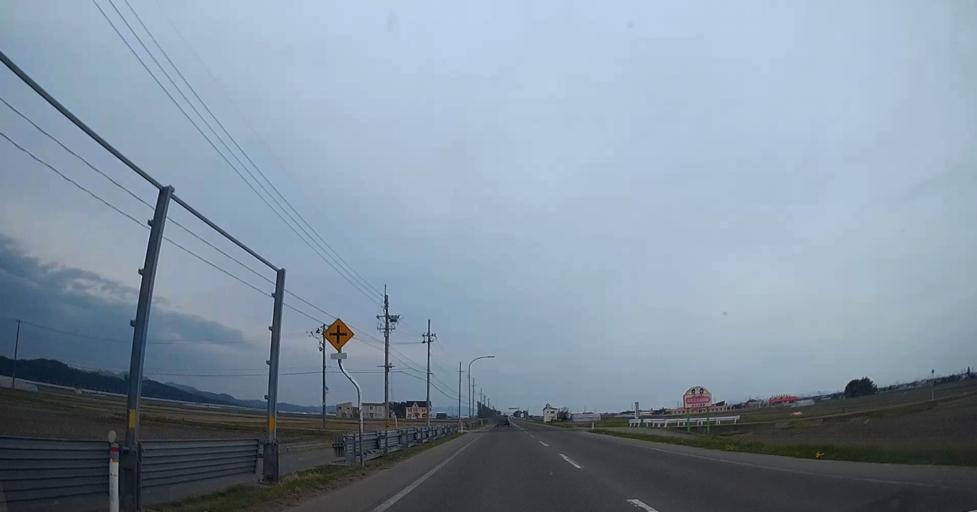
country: JP
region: Aomori
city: Aomori Shi
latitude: 40.8853
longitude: 140.6700
